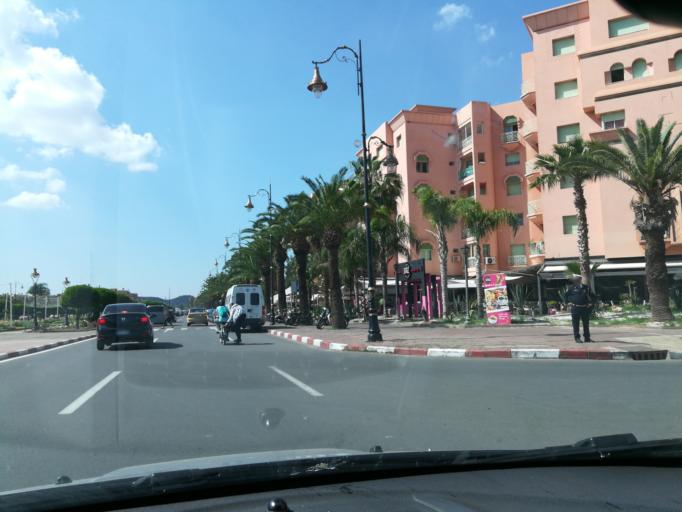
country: MA
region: Marrakech-Tensift-Al Haouz
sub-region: Marrakech
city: Marrakesh
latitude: 31.6247
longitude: -8.0123
